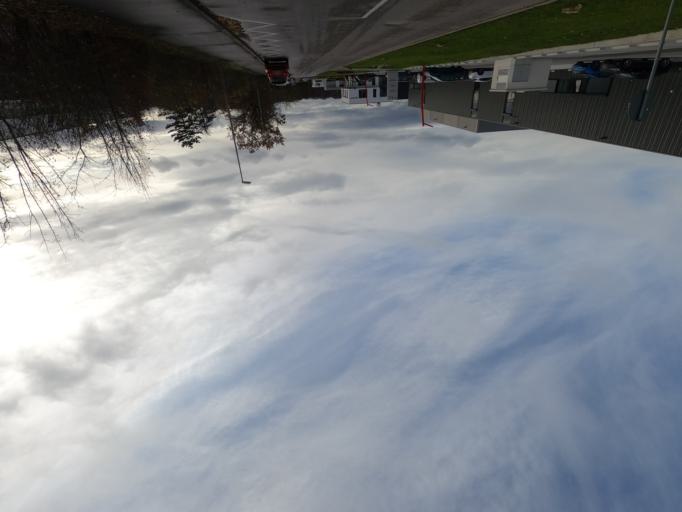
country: DE
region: Baden-Wuerttemberg
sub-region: Regierungsbezirk Stuttgart
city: Schlierbach
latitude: 48.6795
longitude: 9.5345
